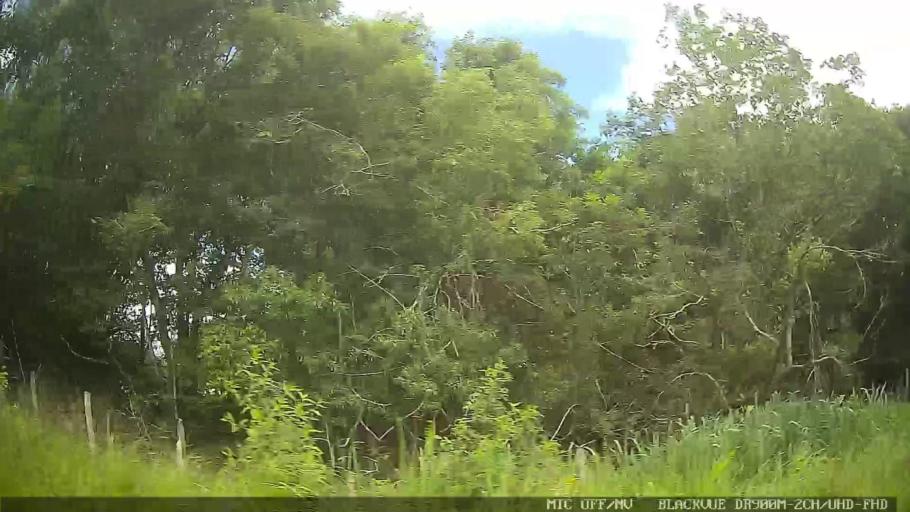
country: BR
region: Sao Paulo
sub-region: Conchas
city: Conchas
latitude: -22.9999
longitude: -47.9997
